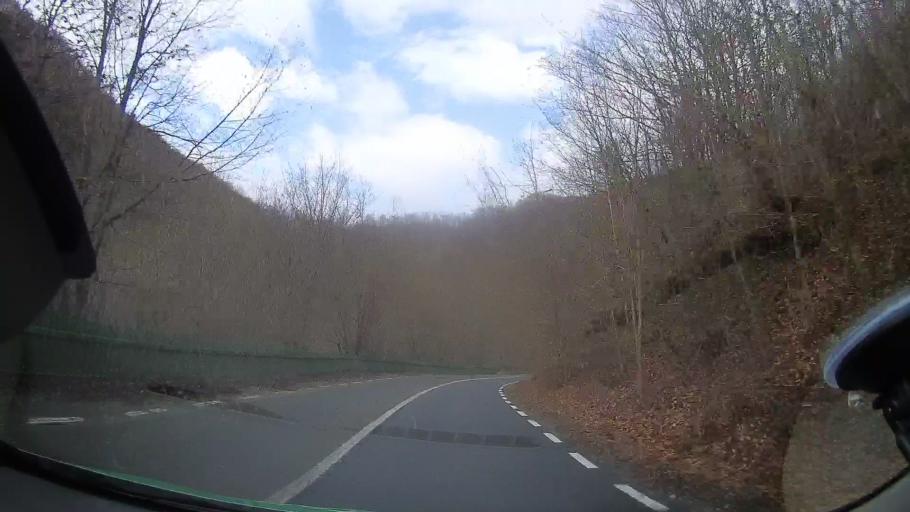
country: RO
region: Cluj
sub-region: Comuna Valea Ierii
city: Valea Ierii
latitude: 46.6288
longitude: 23.3852
